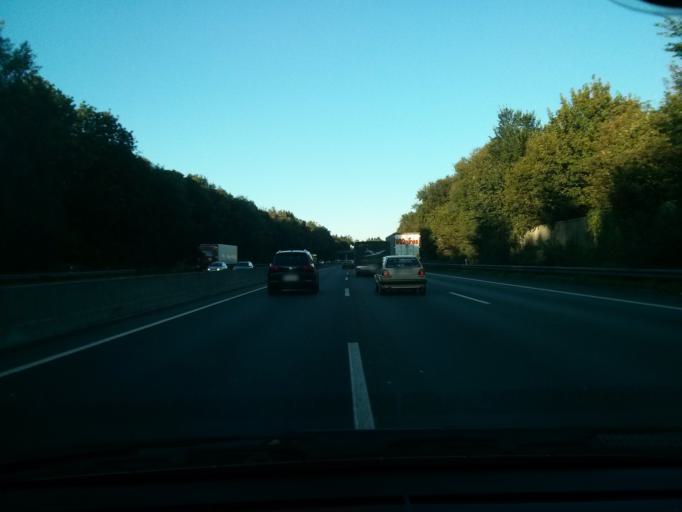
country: DE
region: North Rhine-Westphalia
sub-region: Regierungsbezirk Arnsberg
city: Holzwickede
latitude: 51.4752
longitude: 7.6042
